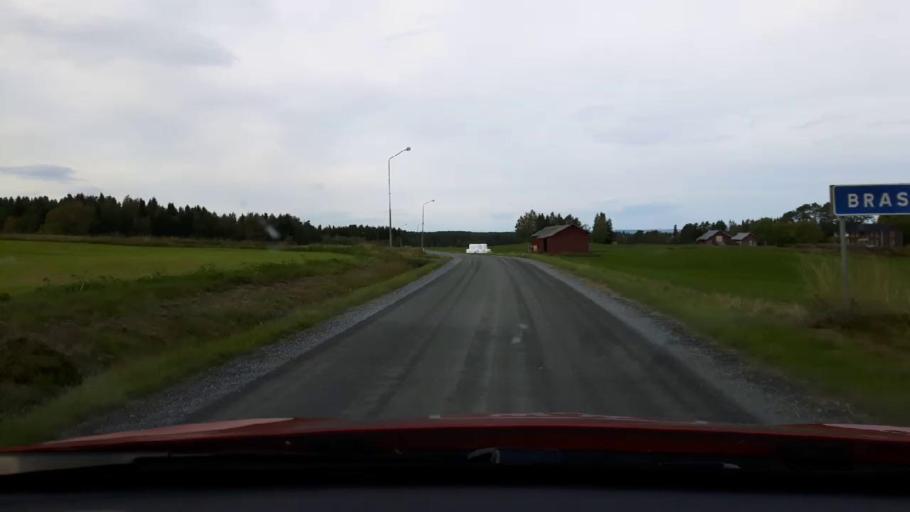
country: SE
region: Jaemtland
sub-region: Krokoms Kommun
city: Valla
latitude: 63.2434
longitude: 13.9940
